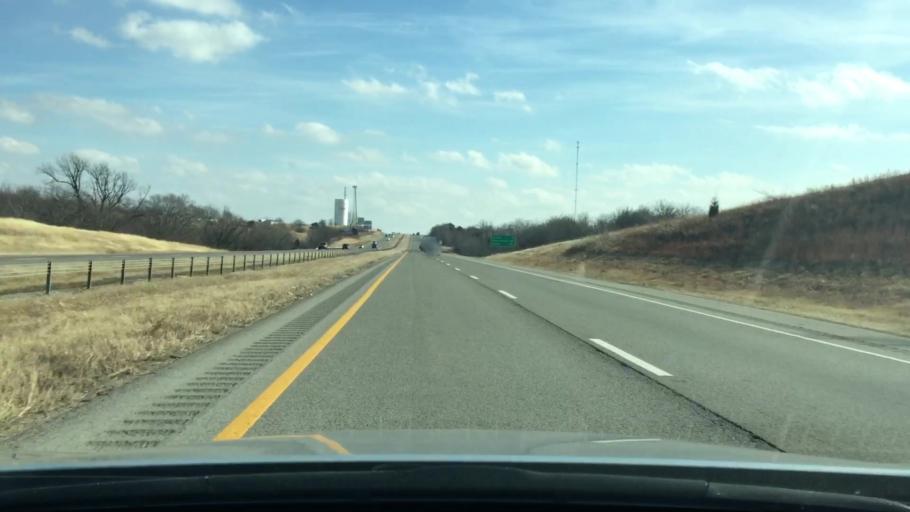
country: US
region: Oklahoma
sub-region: Cleveland County
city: Slaughterville
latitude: 35.0716
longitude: -97.4008
